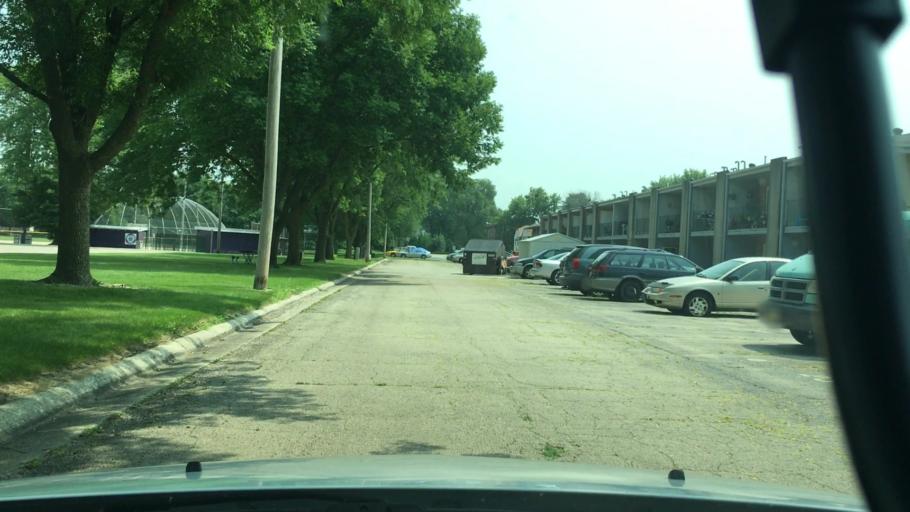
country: US
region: Illinois
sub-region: Ogle County
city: Rochelle
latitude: 41.9265
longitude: -89.0618
